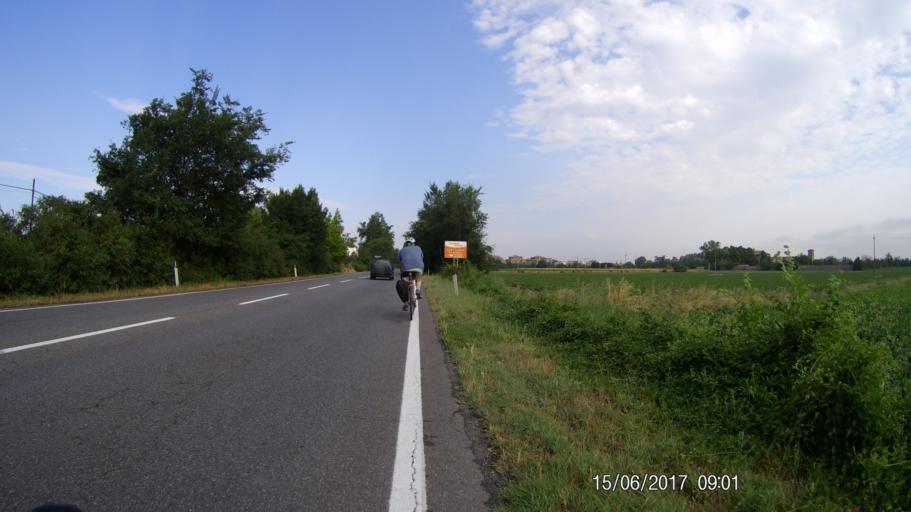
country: IT
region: Emilia-Romagna
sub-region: Provincia di Reggio Emilia
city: Sant'Ilario d'Enza
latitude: 44.7568
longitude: 10.4628
